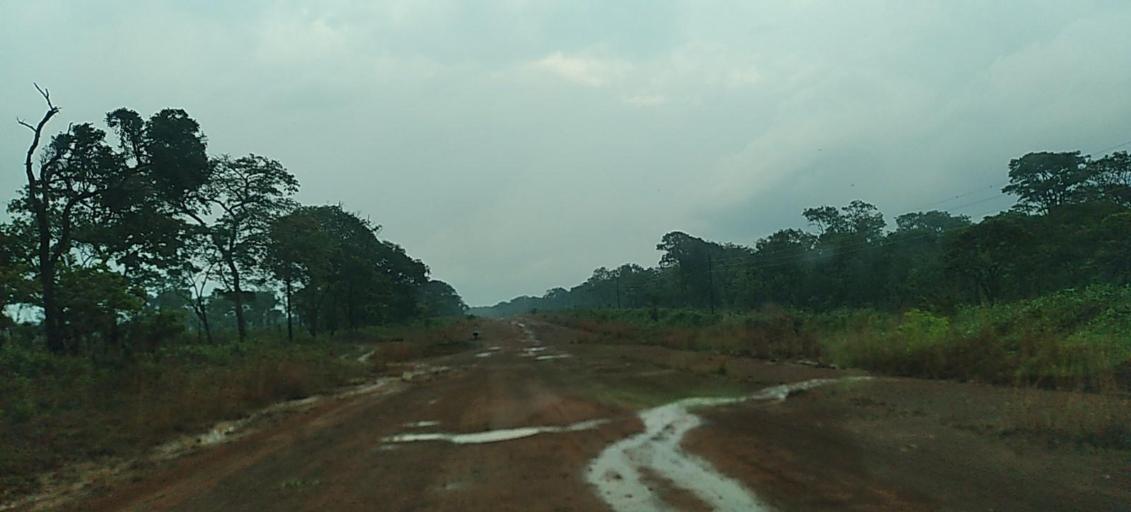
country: ZM
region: North-Western
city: Mwinilunga
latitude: -11.5777
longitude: 24.3920
